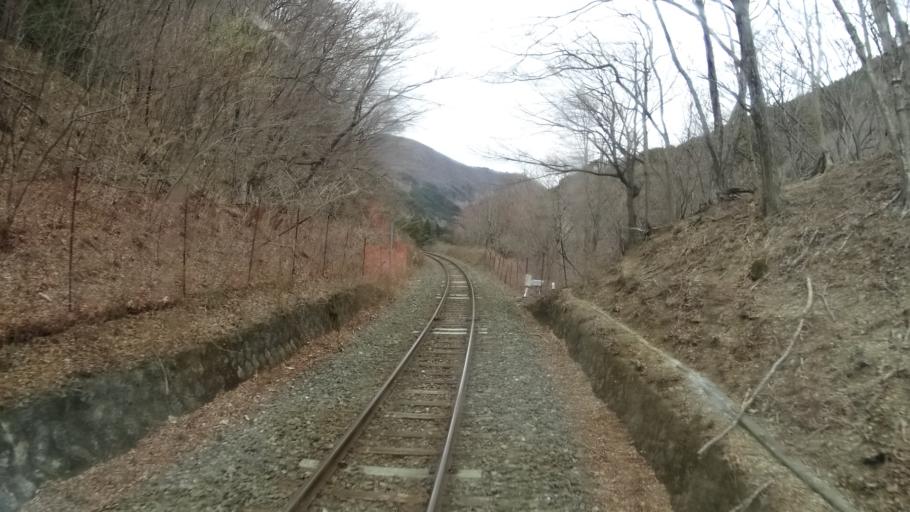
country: JP
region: Iwate
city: Kamaishi
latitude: 39.2549
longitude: 141.7371
